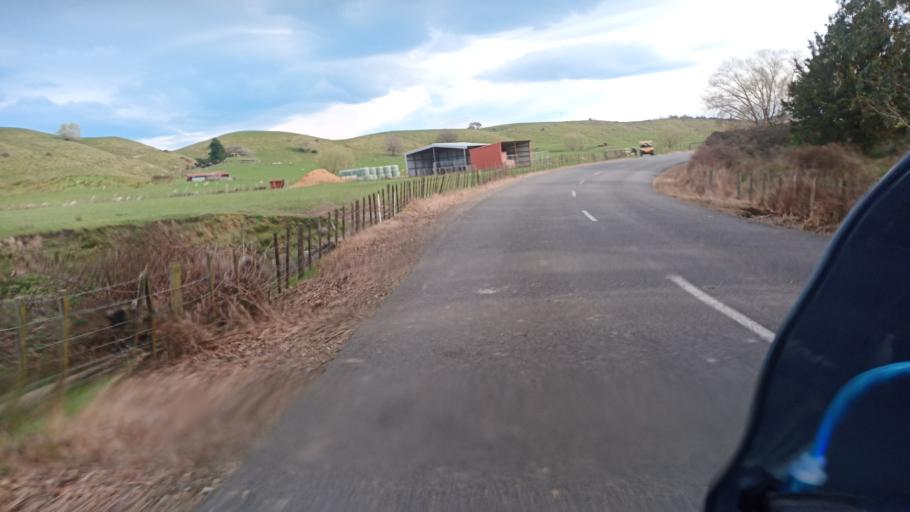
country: NZ
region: Hawke's Bay
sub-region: Wairoa District
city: Wairoa
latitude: -38.9756
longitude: 177.4237
